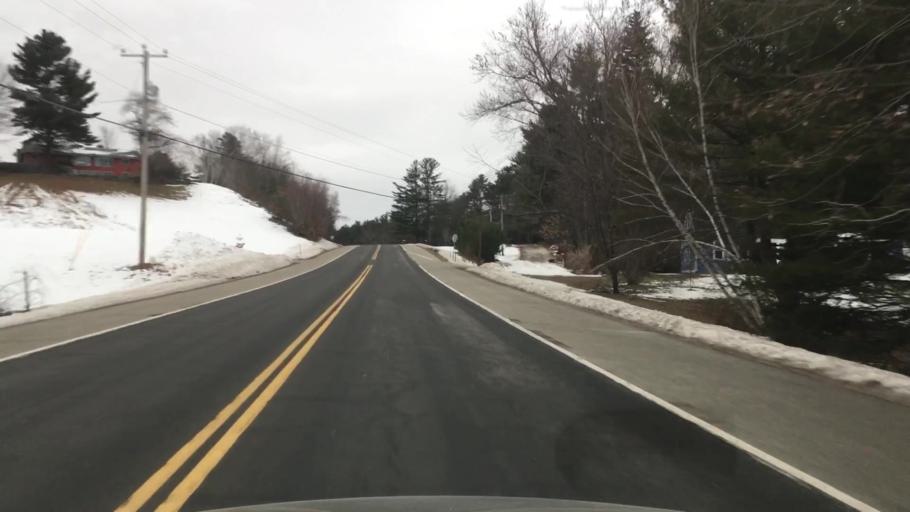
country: US
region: New Hampshire
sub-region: Merrimack County
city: Sutton
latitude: 43.2496
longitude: -71.9248
